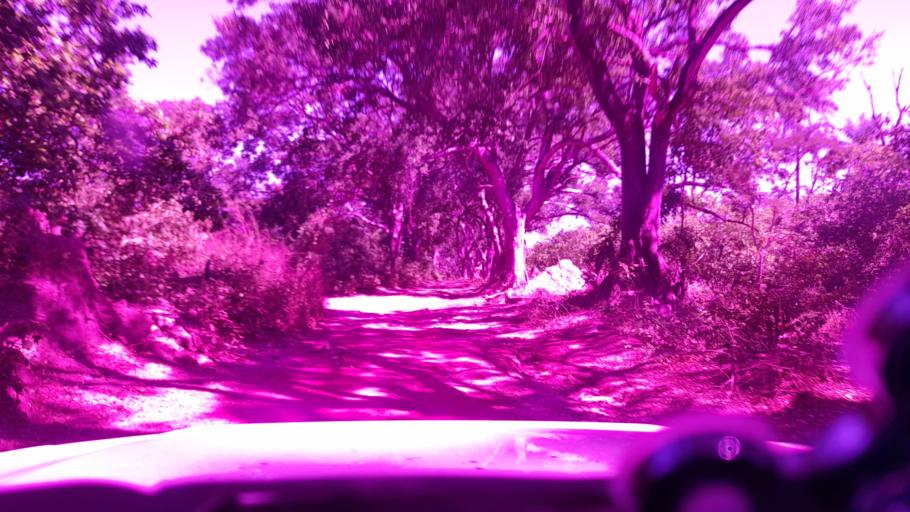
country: GW
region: Oio
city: Bissora
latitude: 12.4344
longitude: -15.5659
